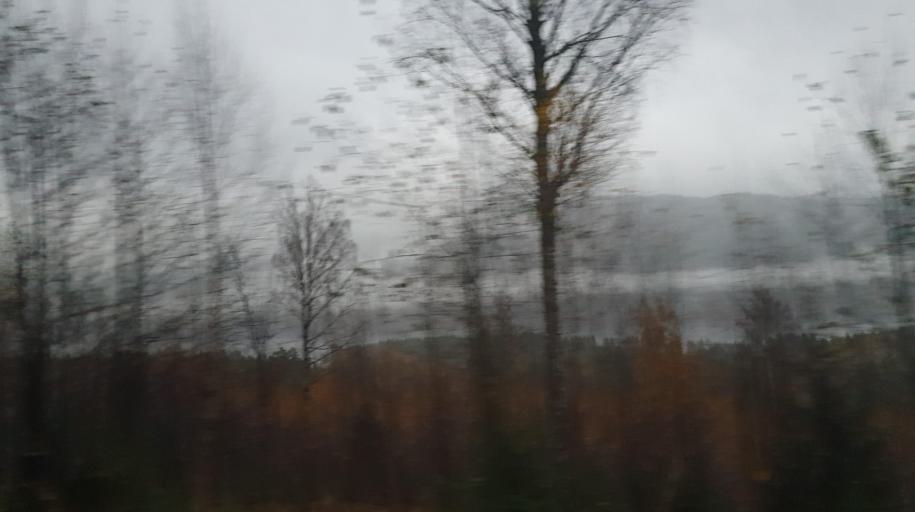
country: NO
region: Buskerud
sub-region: Krodsherad
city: Noresund
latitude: 60.1921
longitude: 9.5931
